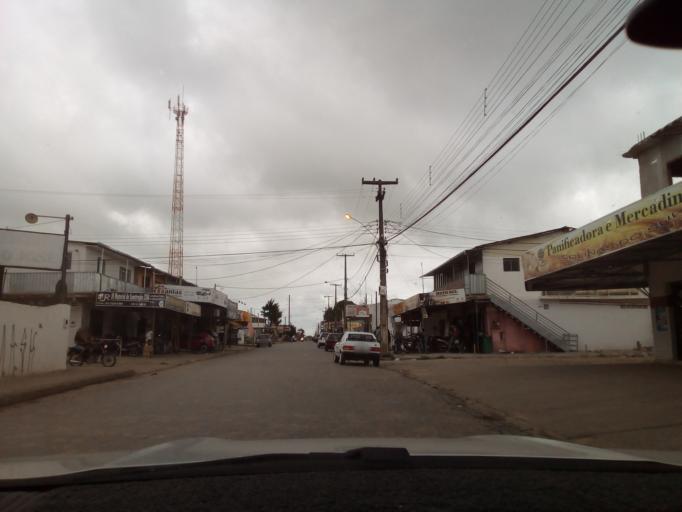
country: BR
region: Paraiba
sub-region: Conde
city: Conde
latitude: -7.1933
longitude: -34.8845
